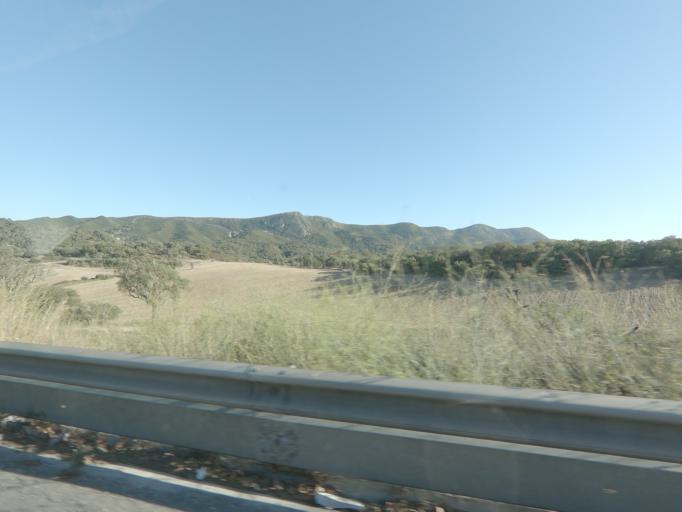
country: PT
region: Setubal
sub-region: Palmela
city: Quinta do Anjo
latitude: 38.5163
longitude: -8.9778
